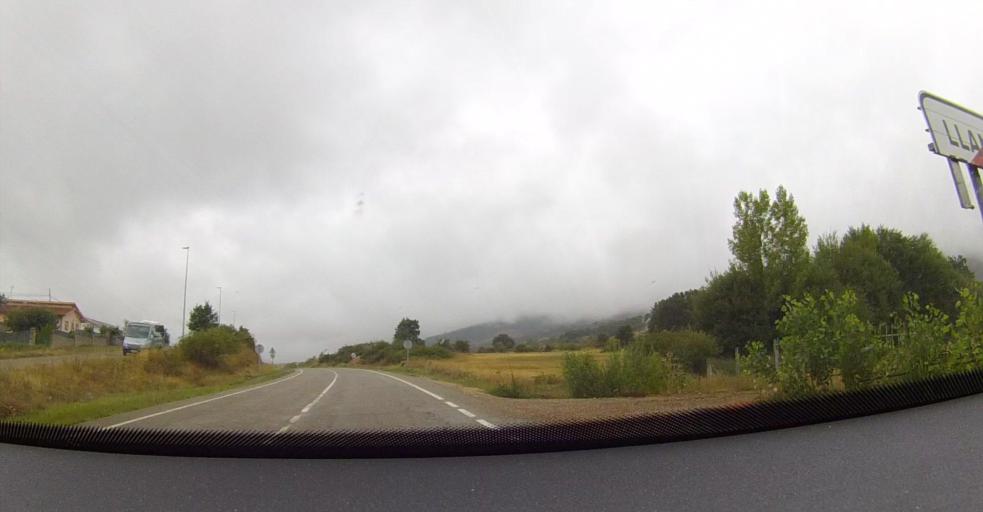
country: ES
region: Castille and Leon
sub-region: Provincia de Leon
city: Bonar
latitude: 42.8417
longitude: -5.2549
